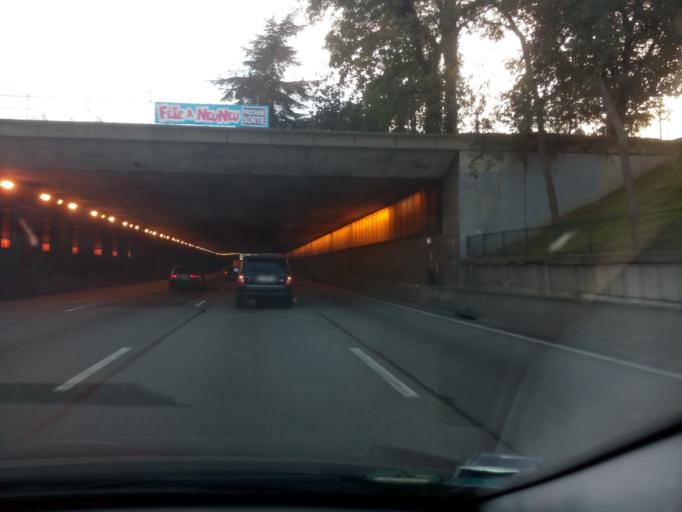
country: FR
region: Ile-de-France
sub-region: Departement des Hauts-de-Seine
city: Neuilly-sur-Seine
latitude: 48.8729
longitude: 2.2744
